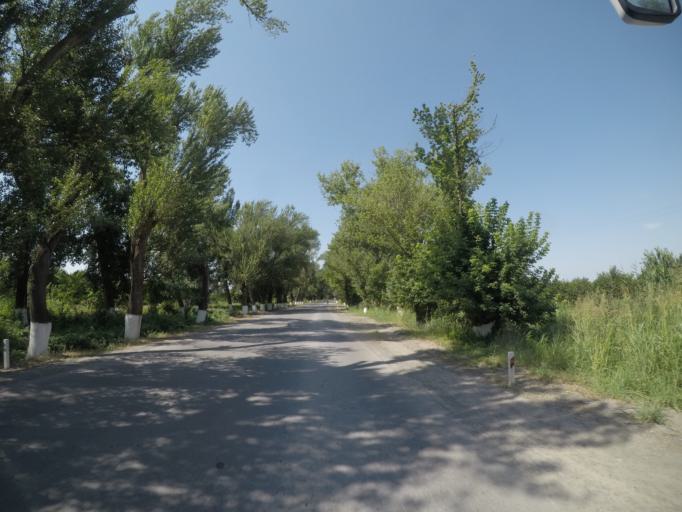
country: AZ
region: Agdas
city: Agdas
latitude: 40.6906
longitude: 47.5365
